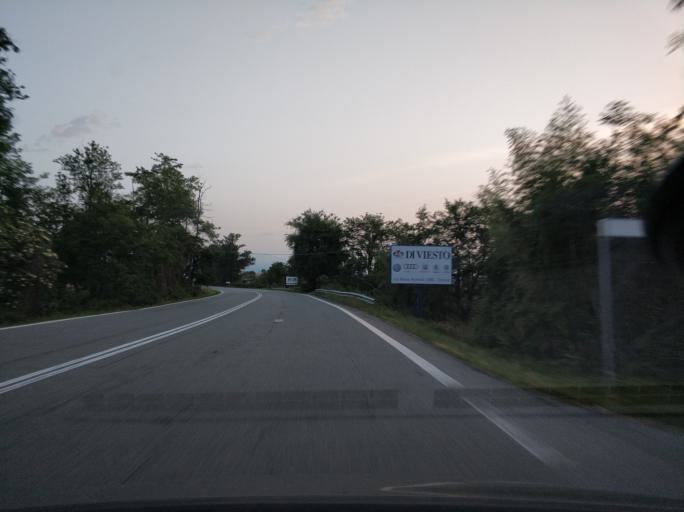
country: IT
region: Piedmont
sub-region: Provincia di Torino
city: Caselle Torinese
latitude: 45.1934
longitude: 7.6407
